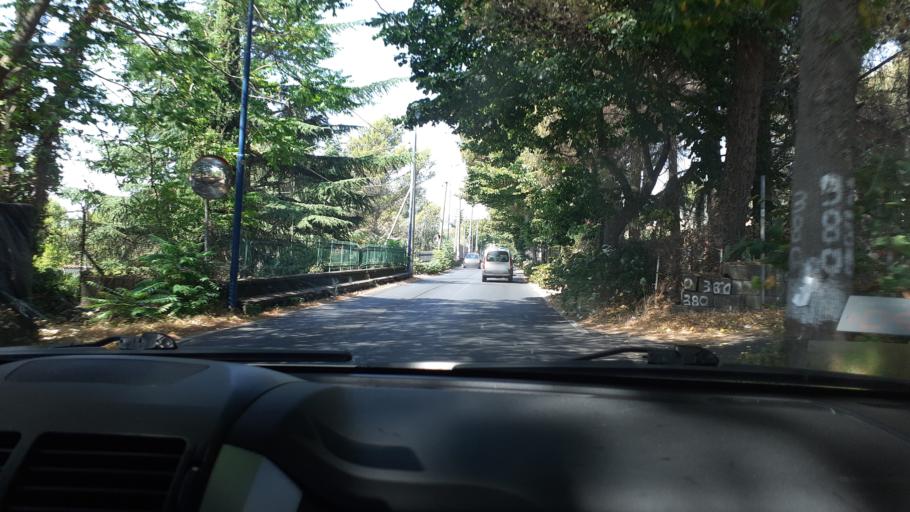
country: IT
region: Sicily
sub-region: Catania
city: Nicolosi
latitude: 37.6152
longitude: 15.0417
